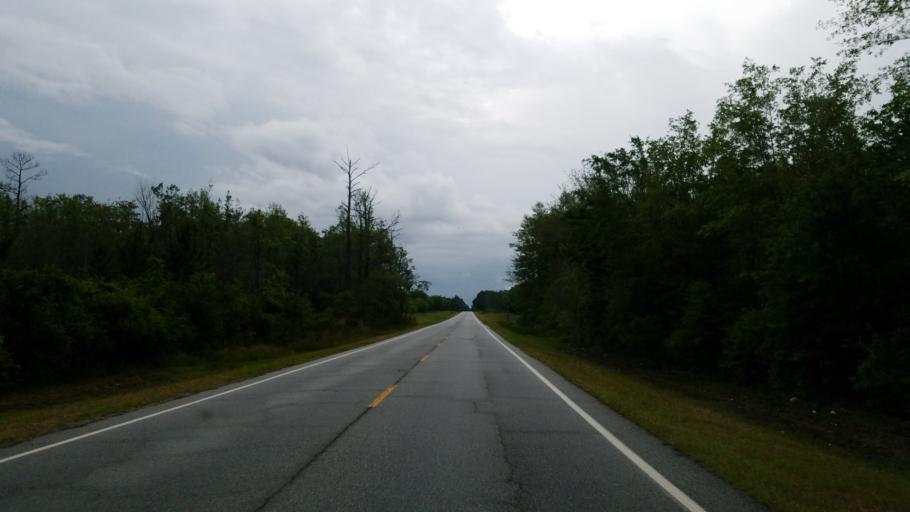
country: US
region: Georgia
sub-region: Berrien County
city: Ray City
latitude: 31.0907
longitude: -83.2498
